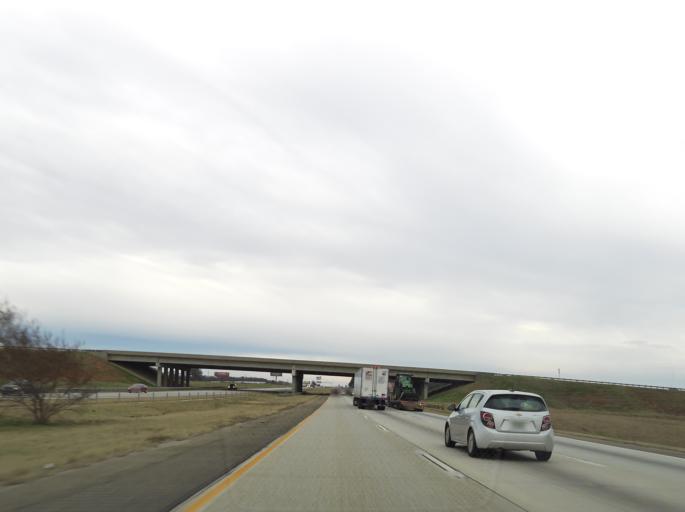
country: US
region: Georgia
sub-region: Peach County
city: Byron
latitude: 32.5883
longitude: -83.7433
